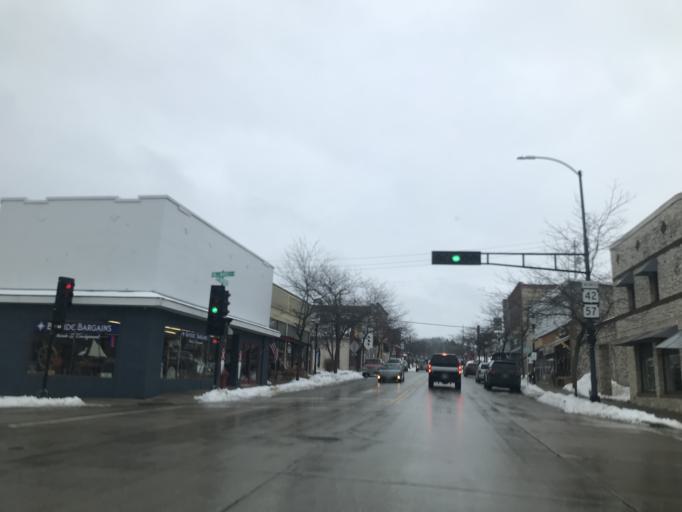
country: US
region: Wisconsin
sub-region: Door County
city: Sturgeon Bay
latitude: 44.8291
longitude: -87.3845
